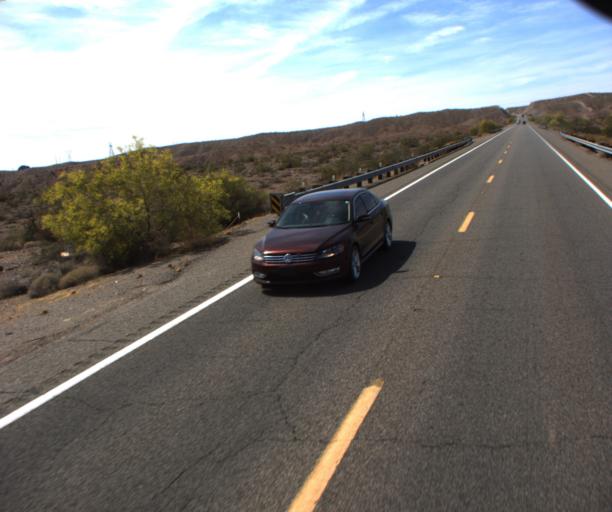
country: US
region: Arizona
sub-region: Mohave County
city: Lake Havasu City
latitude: 34.4202
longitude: -114.2006
